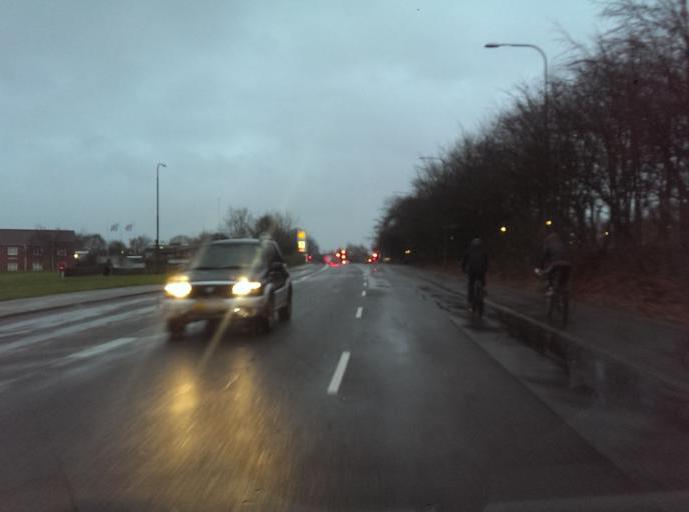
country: DK
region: South Denmark
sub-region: Esbjerg Kommune
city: Esbjerg
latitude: 55.4876
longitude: 8.4464
